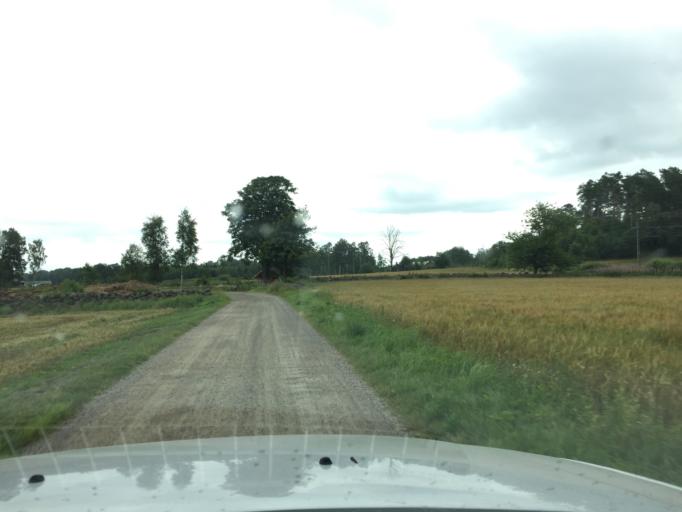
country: SE
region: Skane
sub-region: Hassleholms Kommun
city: Sosdala
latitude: 56.0254
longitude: 13.6618
